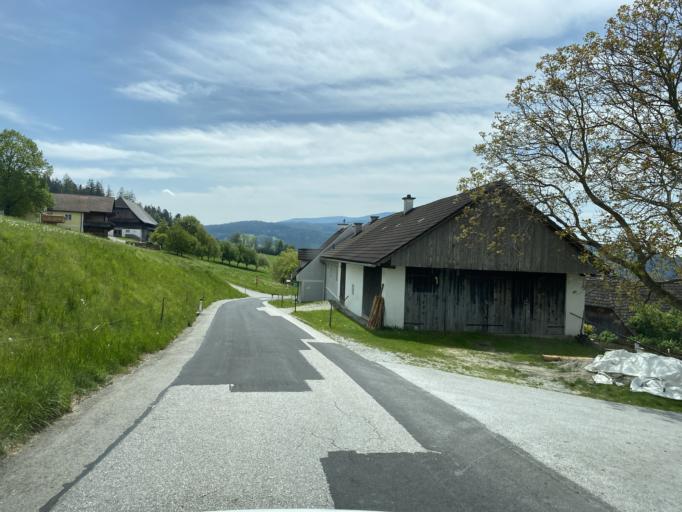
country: AT
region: Styria
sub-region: Politischer Bezirk Weiz
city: Gschaid bei Birkfeld
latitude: 47.3554
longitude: 15.7208
